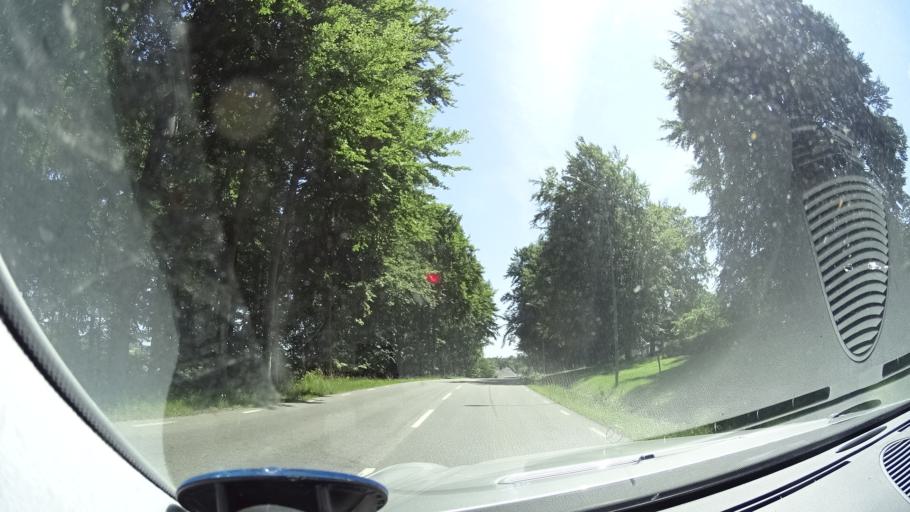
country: SE
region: Skane
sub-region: Kristianstads Kommun
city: Degeberga
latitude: 55.8894
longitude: 14.0121
